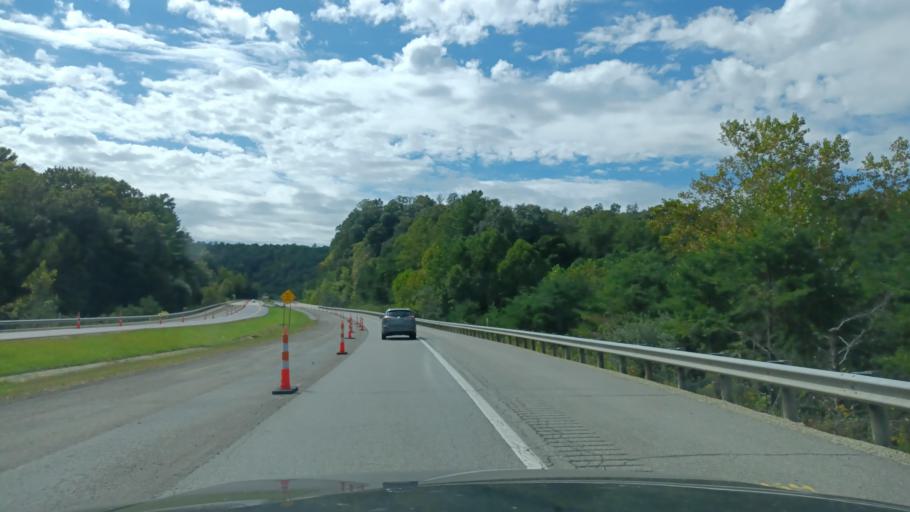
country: US
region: West Virginia
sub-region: Ritchie County
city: Harrisville
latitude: 39.2606
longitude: -81.1031
